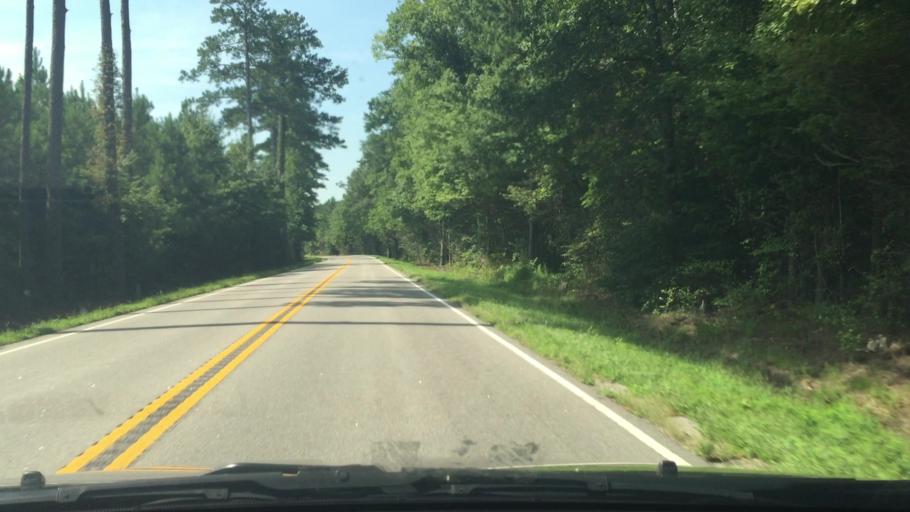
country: US
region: Virginia
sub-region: Southampton County
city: Courtland
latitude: 36.8102
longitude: -77.1271
